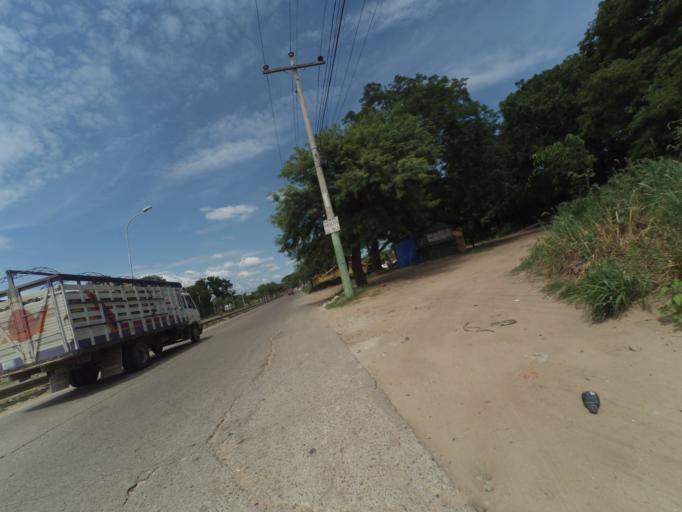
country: BO
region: Santa Cruz
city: Santa Cruz de la Sierra
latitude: -17.7999
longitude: -63.2216
